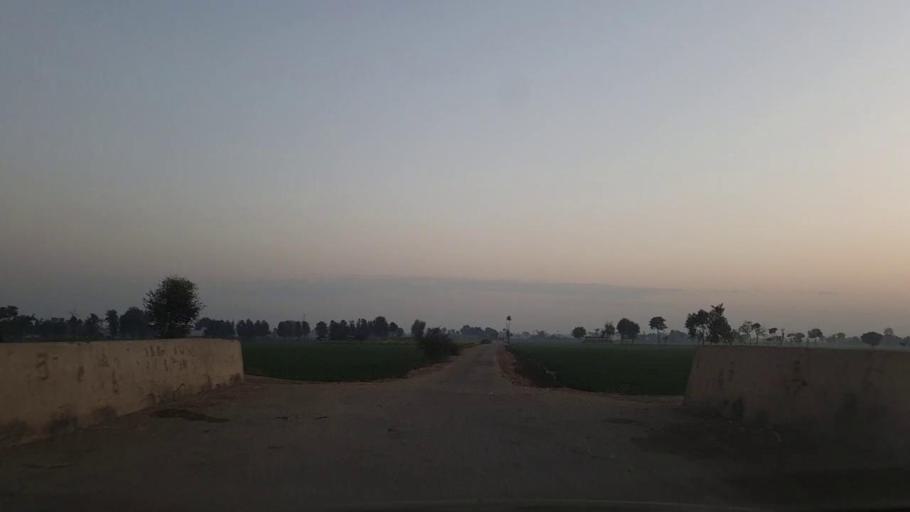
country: PK
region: Sindh
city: Daur
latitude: 26.4809
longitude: 68.4875
